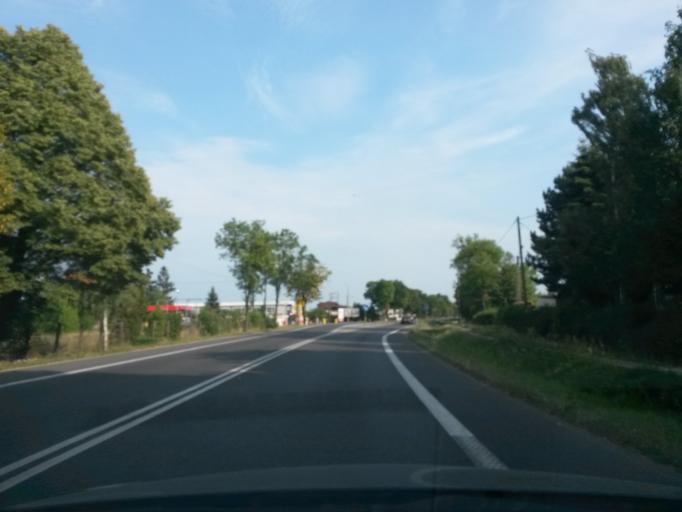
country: PL
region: Masovian Voivodeship
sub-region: Powiat sierpecki
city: Sierpc
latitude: 52.8605
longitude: 19.6779
